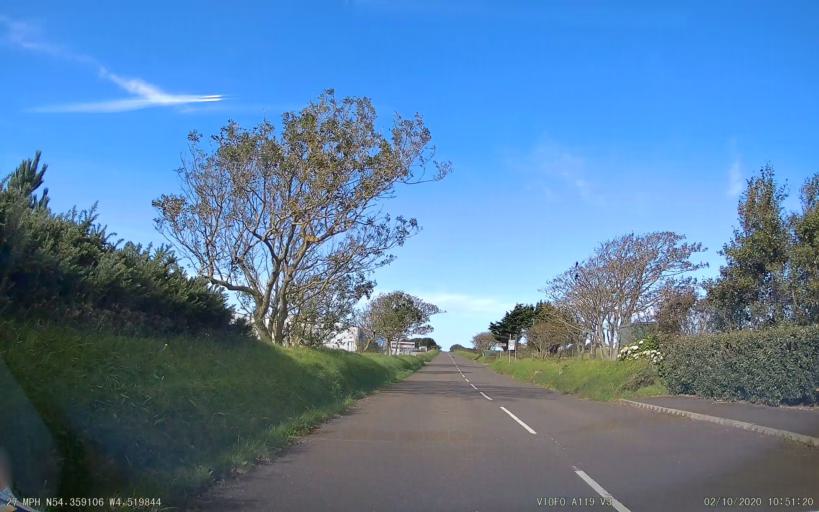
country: IM
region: Ramsey
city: Ramsey
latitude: 54.3591
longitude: -4.5199
